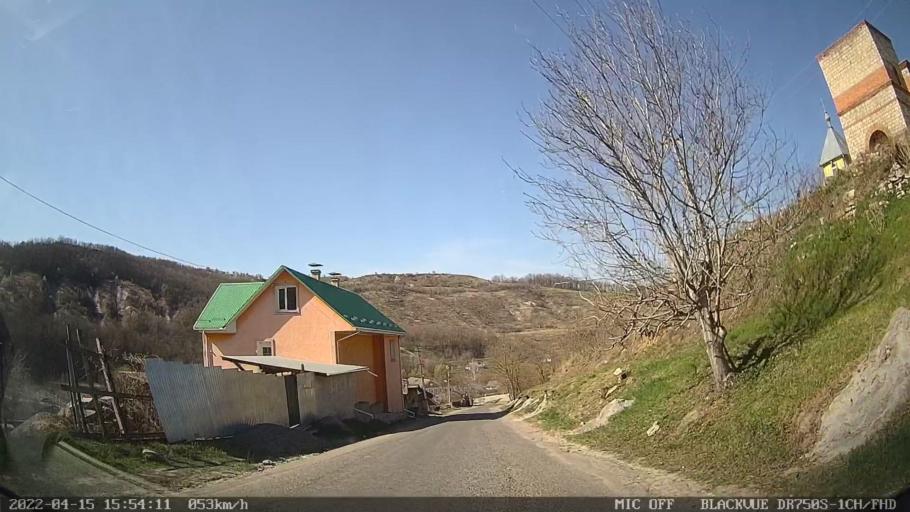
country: MD
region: Raionul Ocnita
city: Otaci
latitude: 48.4022
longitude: 27.8910
